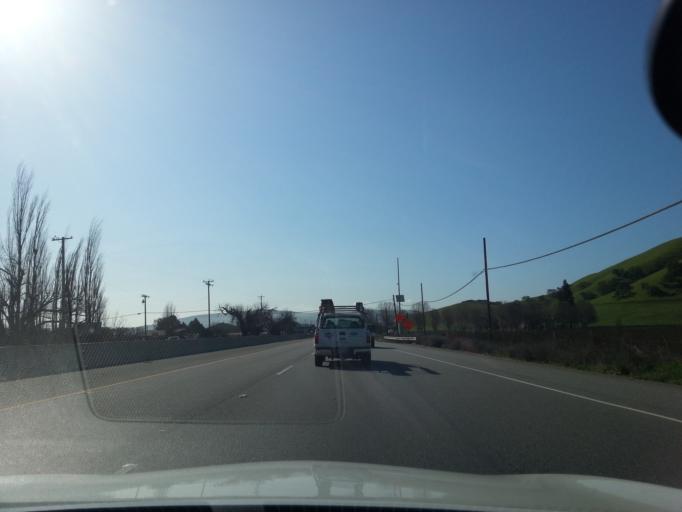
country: US
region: California
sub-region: Santa Clara County
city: Gilroy
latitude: 36.9675
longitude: -121.5529
